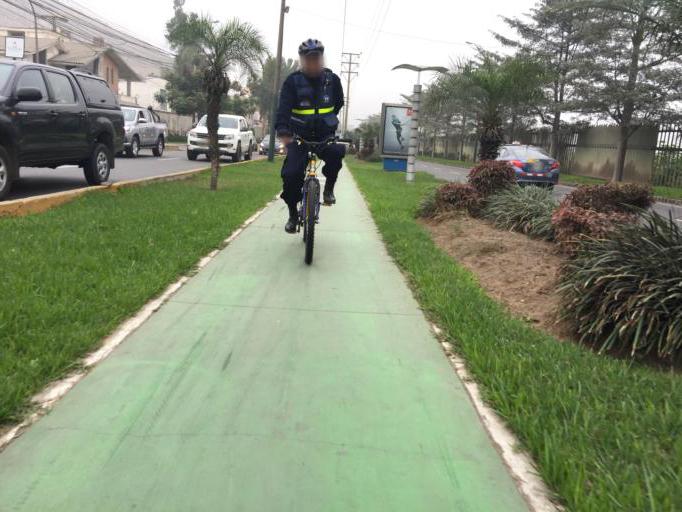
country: PE
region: Lima
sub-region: Lima
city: La Molina
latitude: -12.0842
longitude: -76.9386
